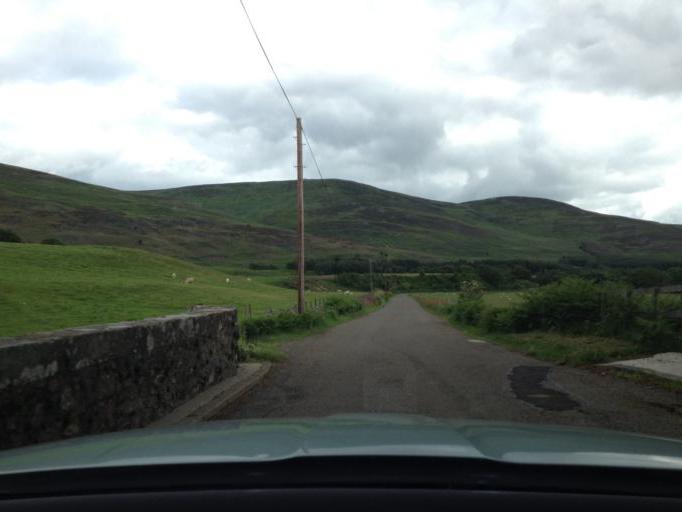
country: GB
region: Scotland
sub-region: Angus
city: Brechin
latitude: 56.8919
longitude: -2.7212
